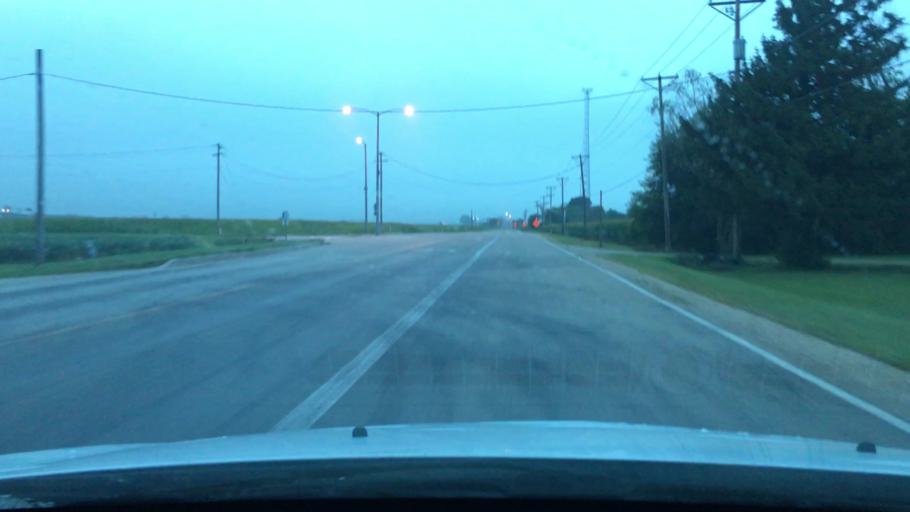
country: US
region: Illinois
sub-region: Ogle County
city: Rochelle
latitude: 41.9198
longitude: -89.0344
